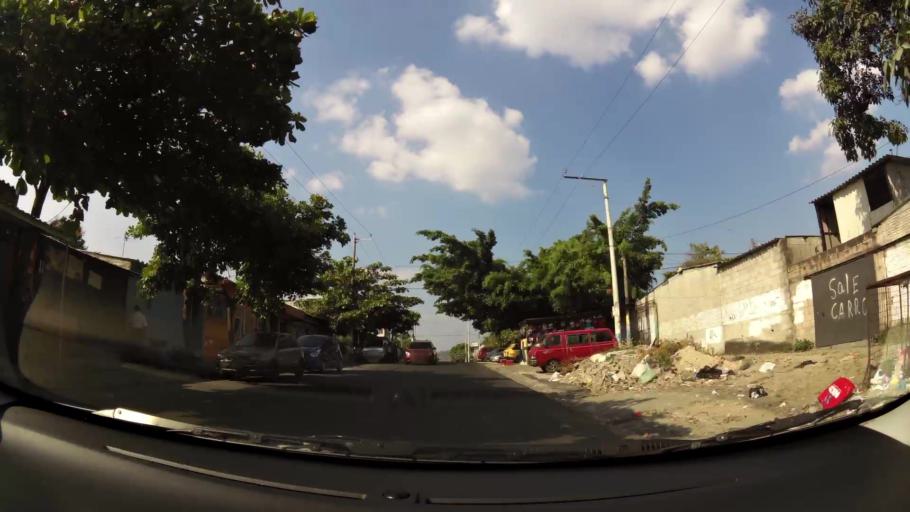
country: SV
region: San Salvador
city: Ilopango
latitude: 13.7175
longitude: -89.1057
